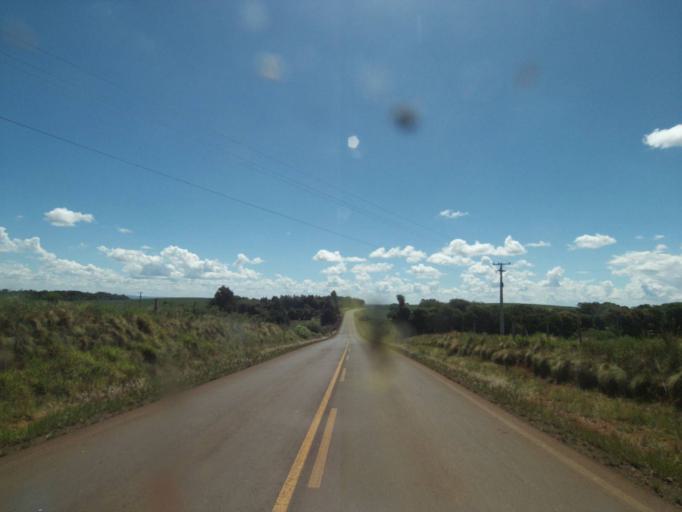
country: BR
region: Parana
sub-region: Pinhao
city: Pinhao
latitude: -25.8132
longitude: -52.0617
